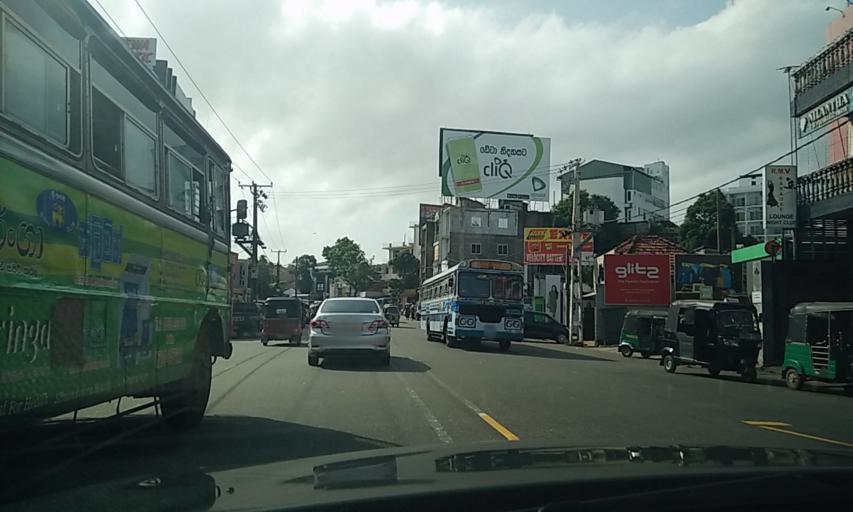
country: LK
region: Western
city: Sri Jayewardenepura Kotte
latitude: 6.8666
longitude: 79.8934
